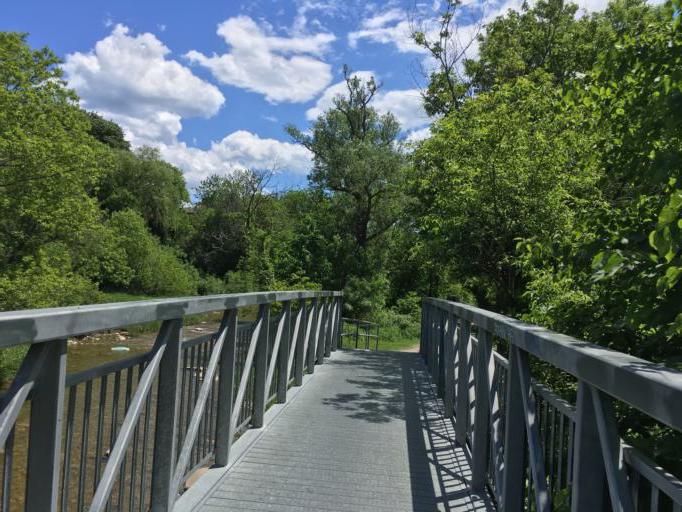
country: CA
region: Ontario
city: Oshawa
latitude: 43.8716
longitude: -78.8479
